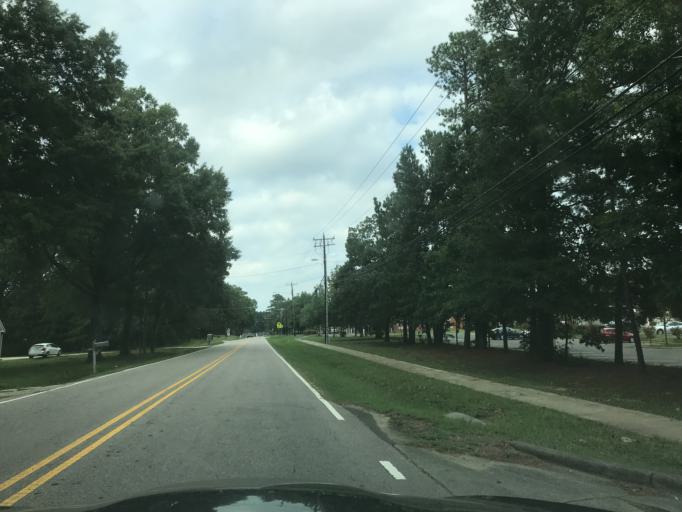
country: US
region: North Carolina
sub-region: Durham County
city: Durham
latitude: 35.9311
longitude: -78.9098
